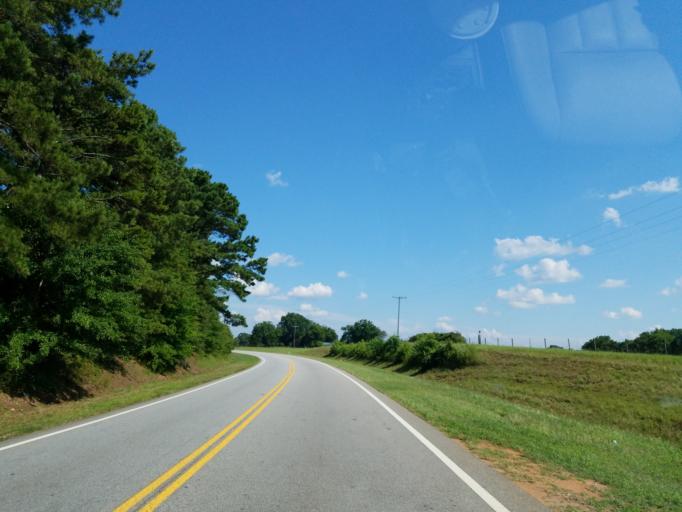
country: US
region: Georgia
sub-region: Crawford County
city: Roberta
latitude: 32.8086
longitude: -84.0506
